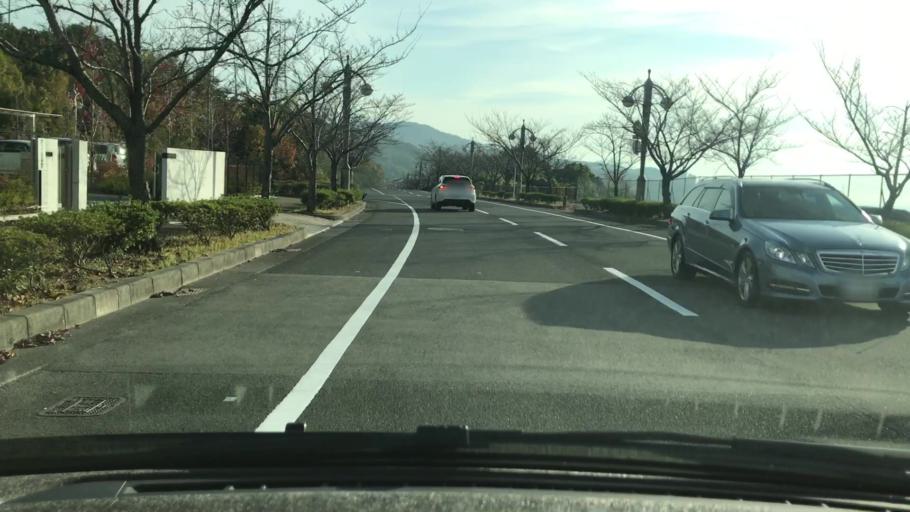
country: JP
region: Hyogo
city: Takarazuka
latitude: 34.8344
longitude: 135.3013
